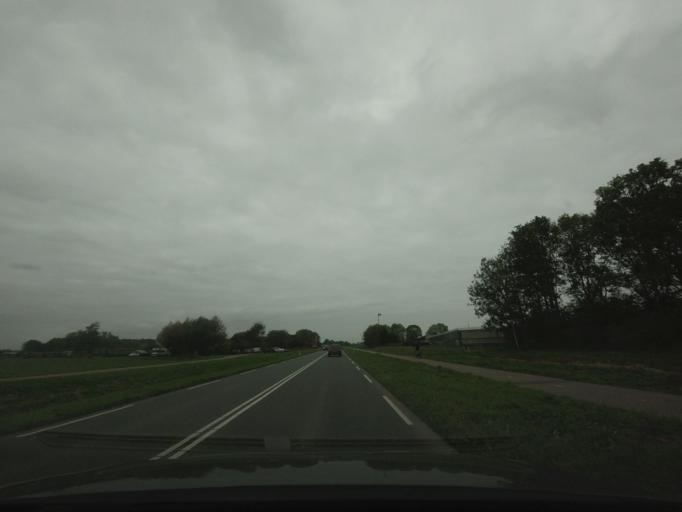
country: NL
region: North Holland
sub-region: Gemeente Heerhugowaard
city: Heerhugowaard
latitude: 52.6732
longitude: 4.8897
